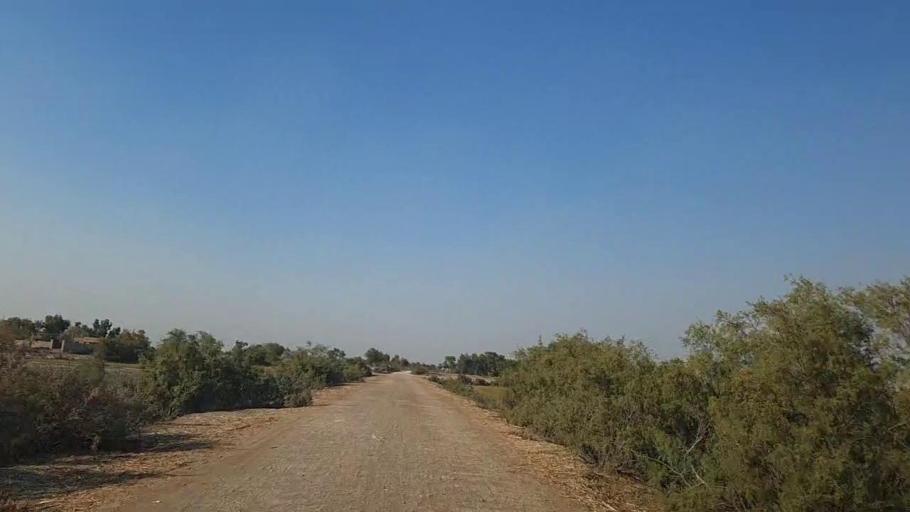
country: PK
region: Sindh
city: Daur
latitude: 26.3241
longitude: 68.1781
